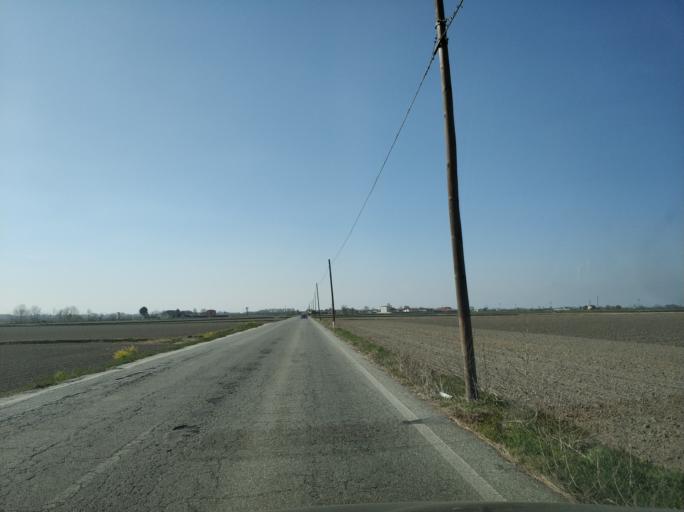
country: IT
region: Piedmont
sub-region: Provincia di Novara
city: Vinzaglio
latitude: 45.3171
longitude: 8.4913
